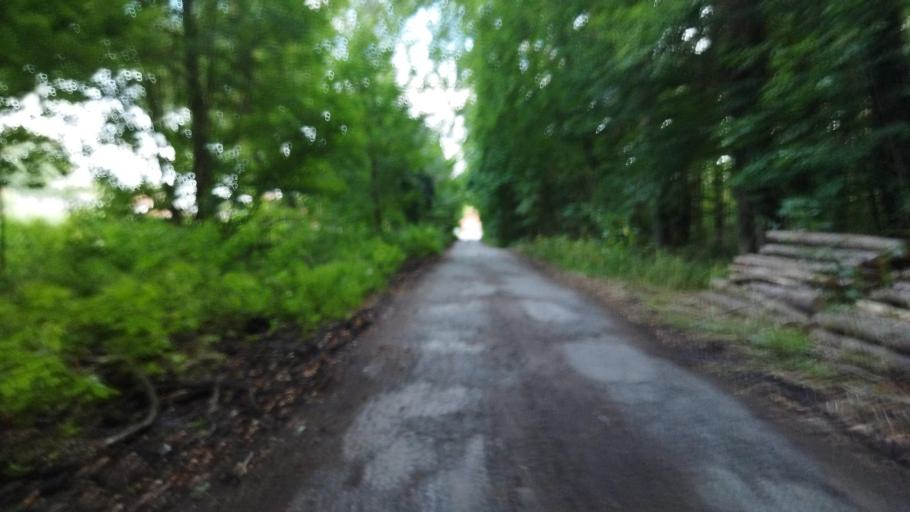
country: DE
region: Lower Saxony
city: Glandorf
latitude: 52.0890
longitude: 8.0344
